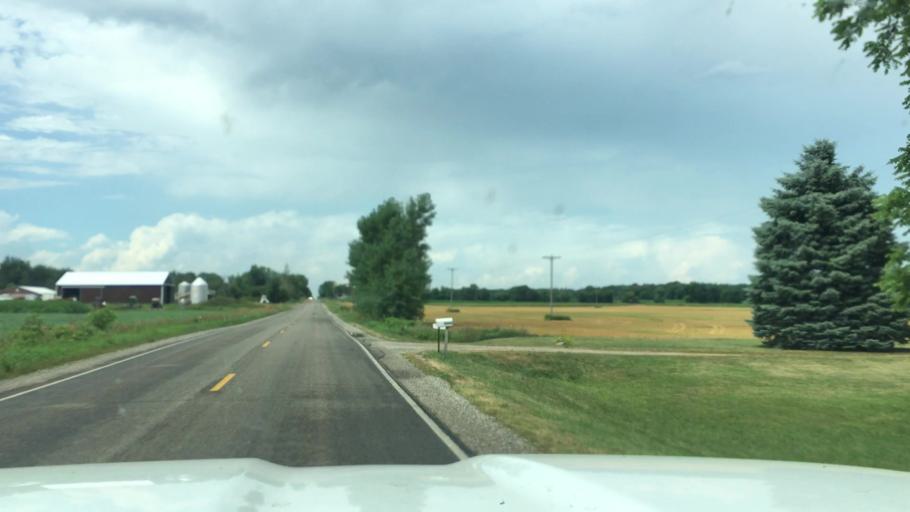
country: US
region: Michigan
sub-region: Montcalm County
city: Carson City
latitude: 43.2304
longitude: -84.7776
